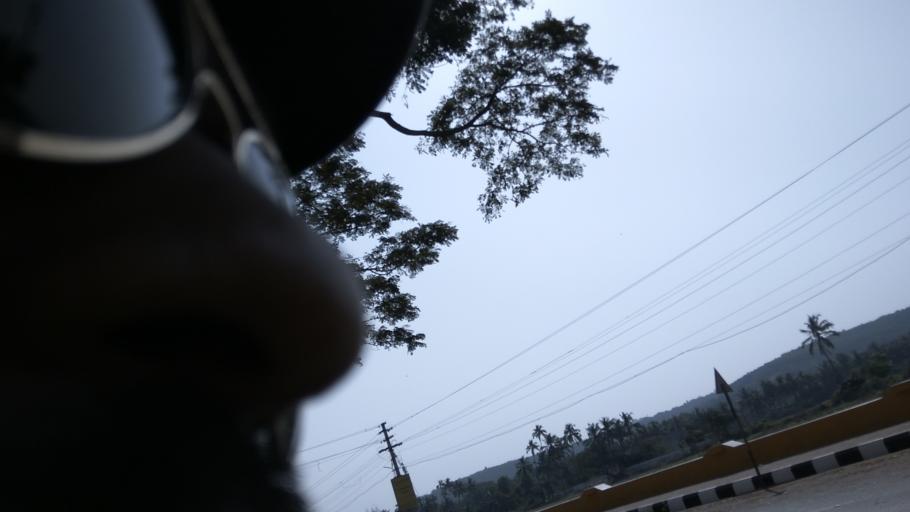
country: IN
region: Goa
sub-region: North Goa
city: Saligao
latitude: 15.5460
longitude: 73.7857
